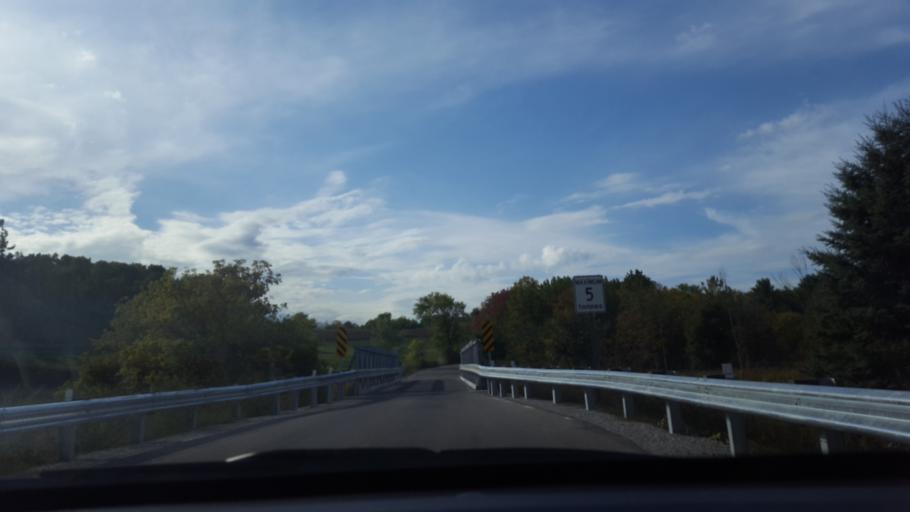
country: CA
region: Ontario
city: Vaughan
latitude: 43.8839
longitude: -79.6341
